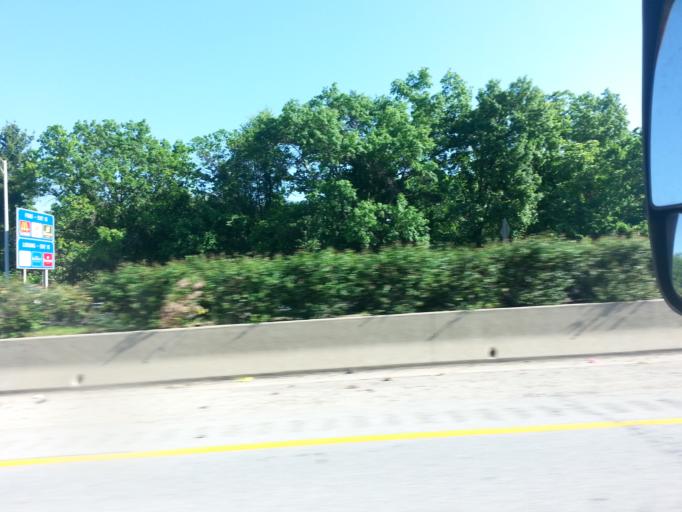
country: US
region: Kentucky
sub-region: Jefferson County
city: Douglass Hills
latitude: 38.2234
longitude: -85.5510
